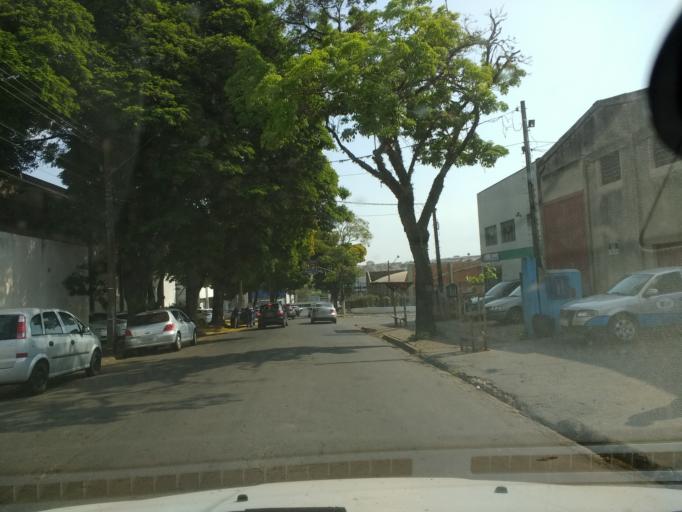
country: BR
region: Parana
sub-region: Londrina
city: Londrina
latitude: -23.2942
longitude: -51.1615
